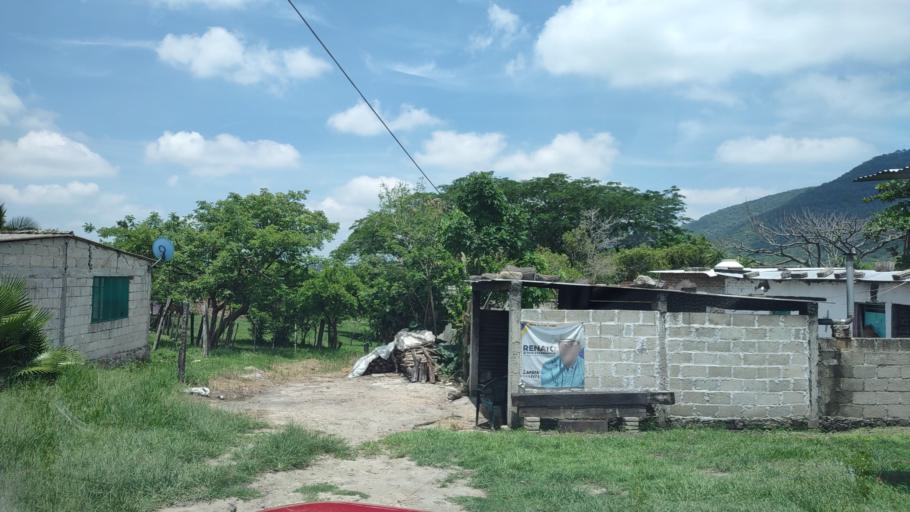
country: MX
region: Veracruz
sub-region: Emiliano Zapata
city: Dos Rios
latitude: 19.4281
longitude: -96.8054
